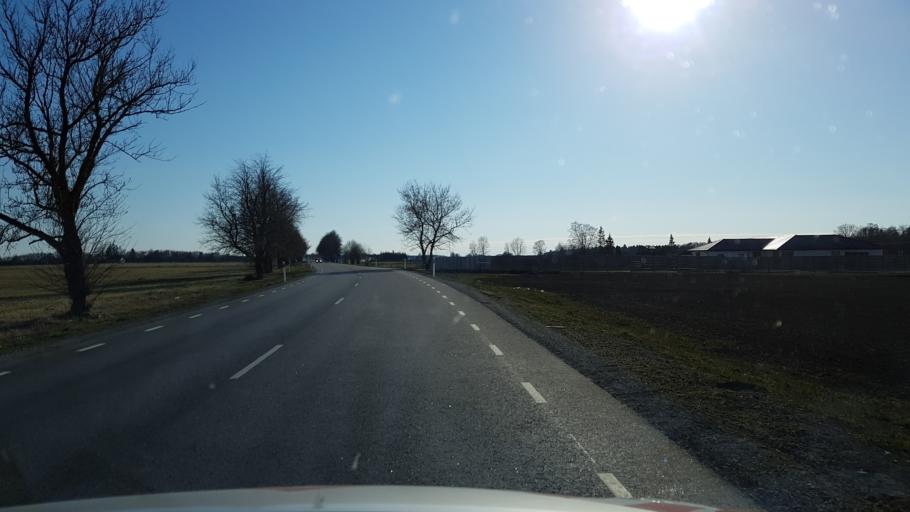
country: EE
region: Ida-Virumaa
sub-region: Johvi vald
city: Johvi
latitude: 59.3482
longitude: 27.3721
